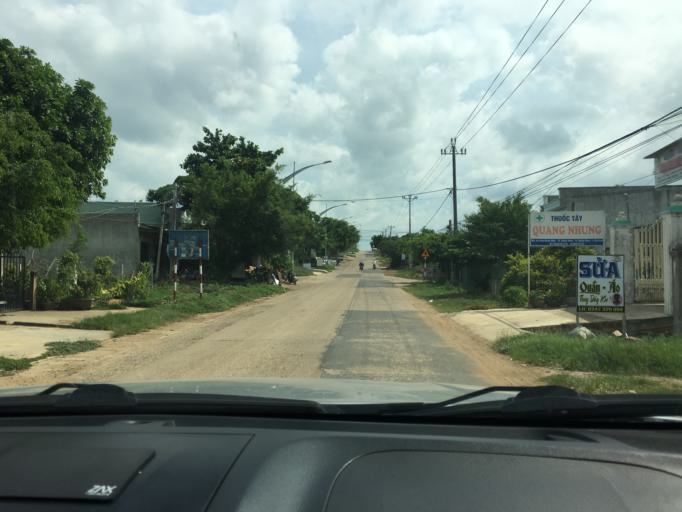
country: VN
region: Gia Lai
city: Kong Chro
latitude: 13.7793
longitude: 108.5182
